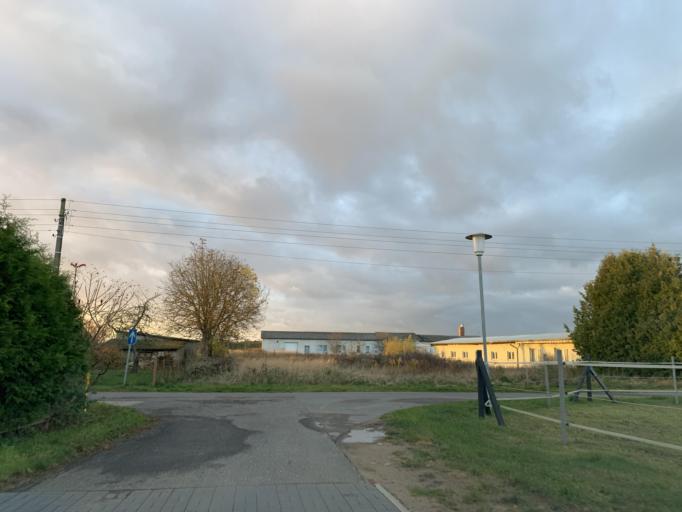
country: DE
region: Mecklenburg-Vorpommern
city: Blankensee
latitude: 53.4004
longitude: 13.2883
